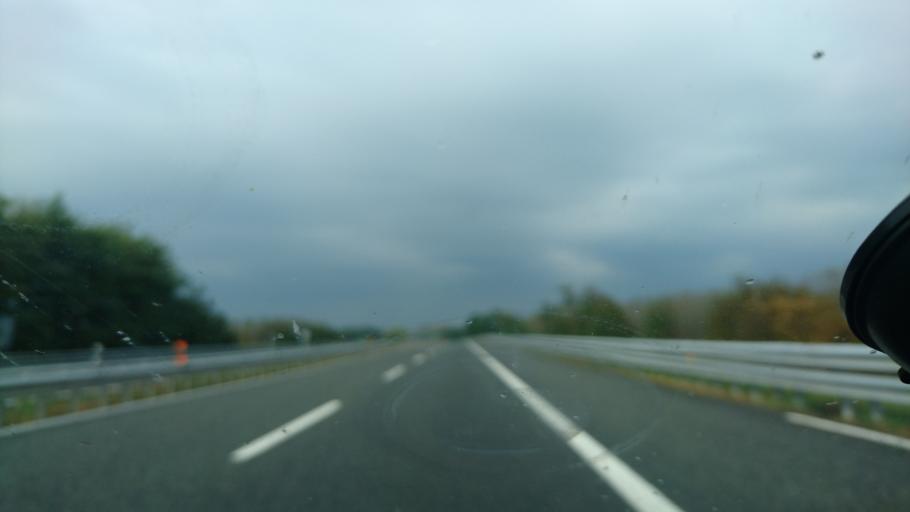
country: IT
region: Piedmont
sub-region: Provincia di Novara
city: Sillavengo
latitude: 45.5283
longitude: 8.4319
